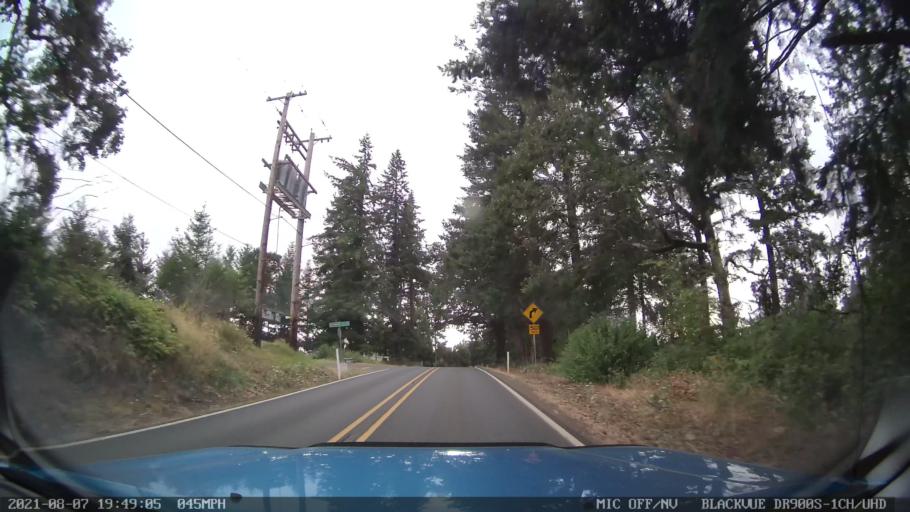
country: US
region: Oregon
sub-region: Marion County
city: Silverton
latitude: 44.9800
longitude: -122.7217
